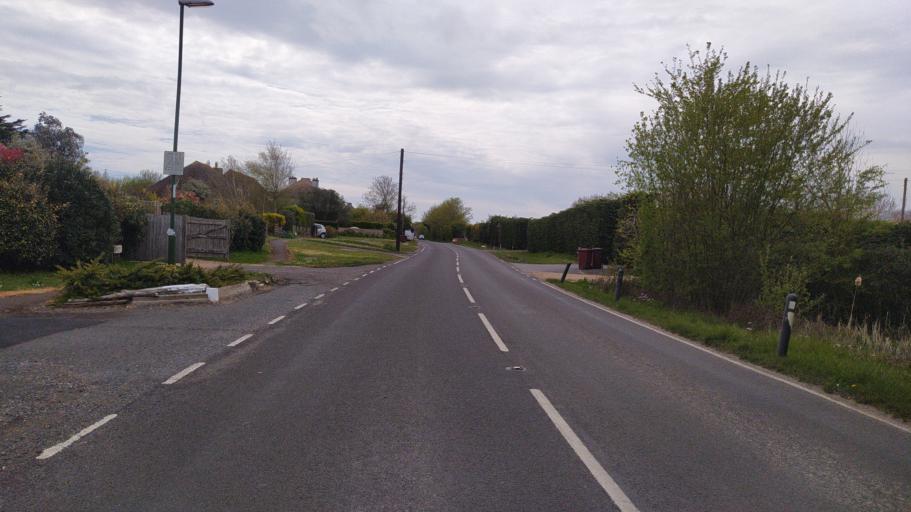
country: GB
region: England
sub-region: West Sussex
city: East Wittering
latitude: 50.7724
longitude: -0.8519
